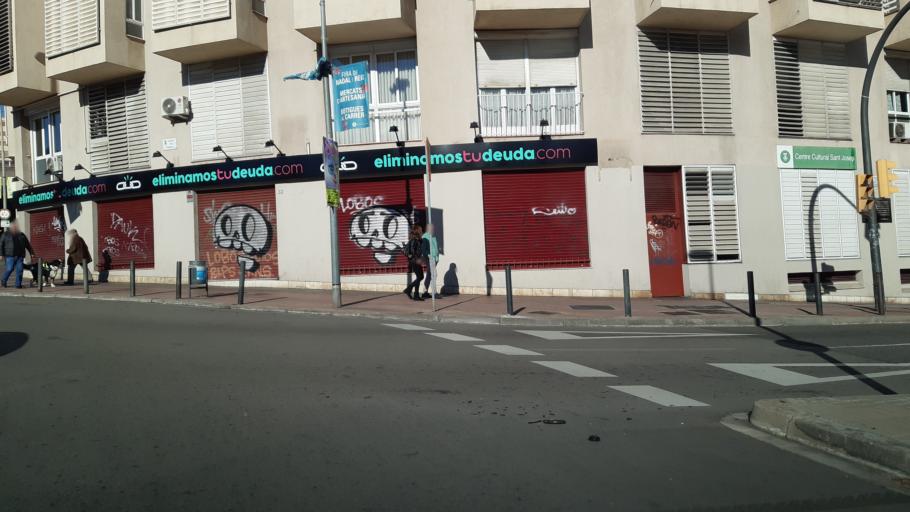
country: ES
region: Catalonia
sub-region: Provincia de Barcelona
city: L'Hospitalet de Llobregat
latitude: 41.3636
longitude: 2.1051
